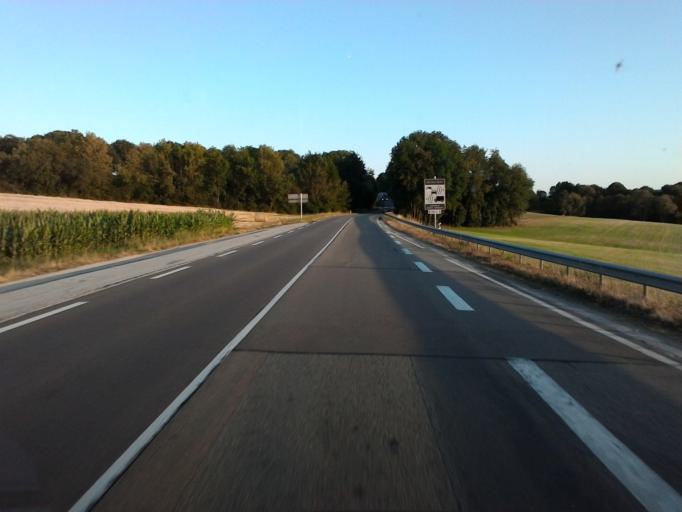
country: FR
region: Franche-Comte
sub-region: Departement du Doubs
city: Quingey
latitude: 47.0784
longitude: 5.8829
